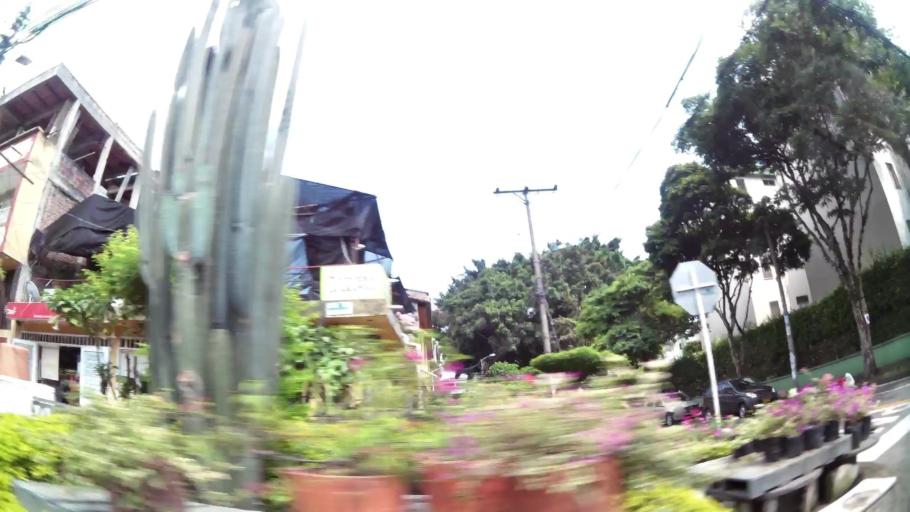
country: CO
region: Valle del Cauca
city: Cali
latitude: 3.4070
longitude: -76.5322
